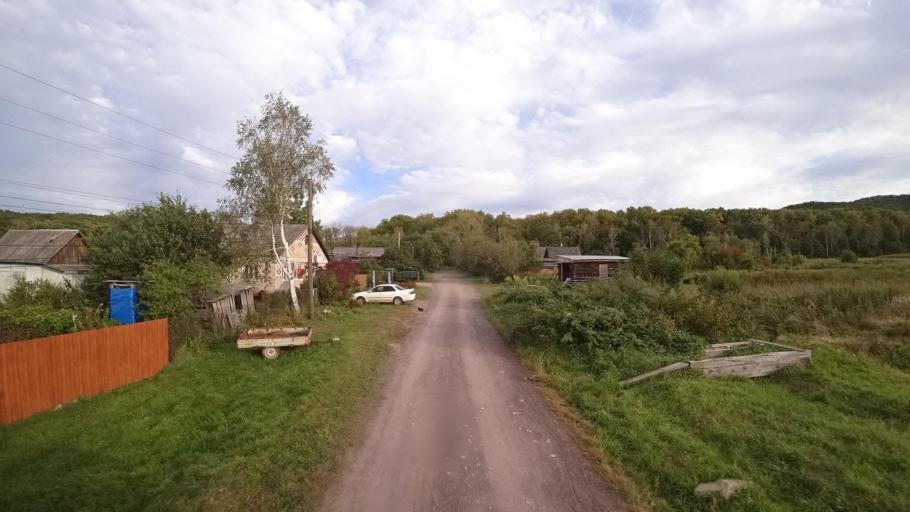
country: RU
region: Primorskiy
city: Yakovlevka
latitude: 44.4126
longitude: 133.4491
